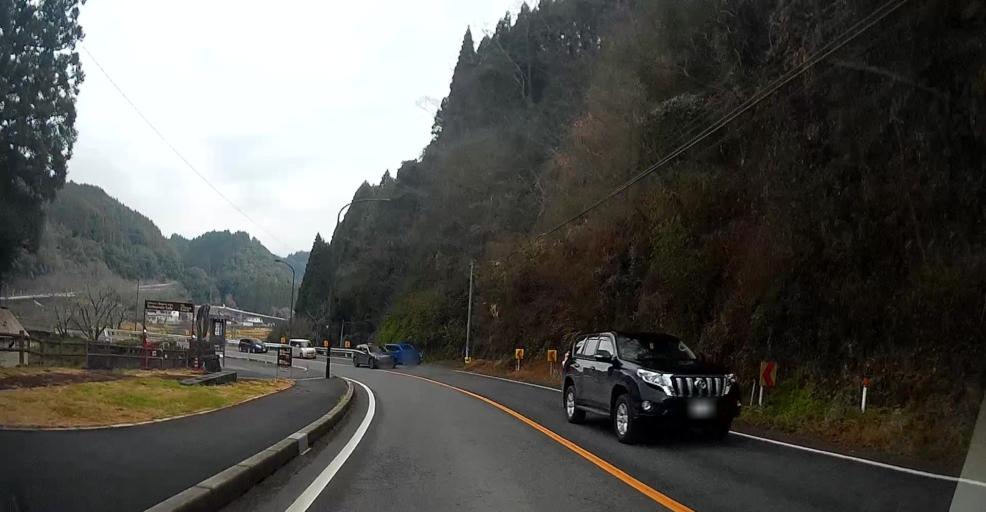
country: JP
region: Kumamoto
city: Matsubase
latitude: 32.6284
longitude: 130.8884
